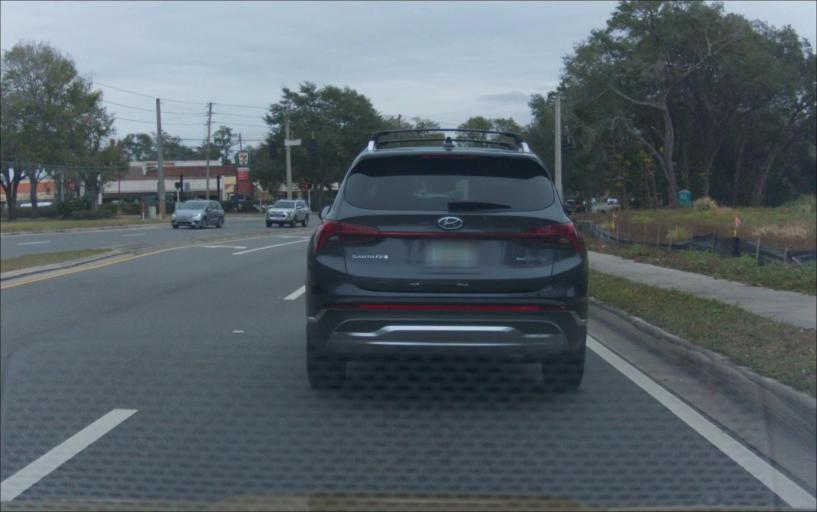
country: US
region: Florida
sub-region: Orange County
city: Winter Park
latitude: 28.6237
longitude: -81.3192
